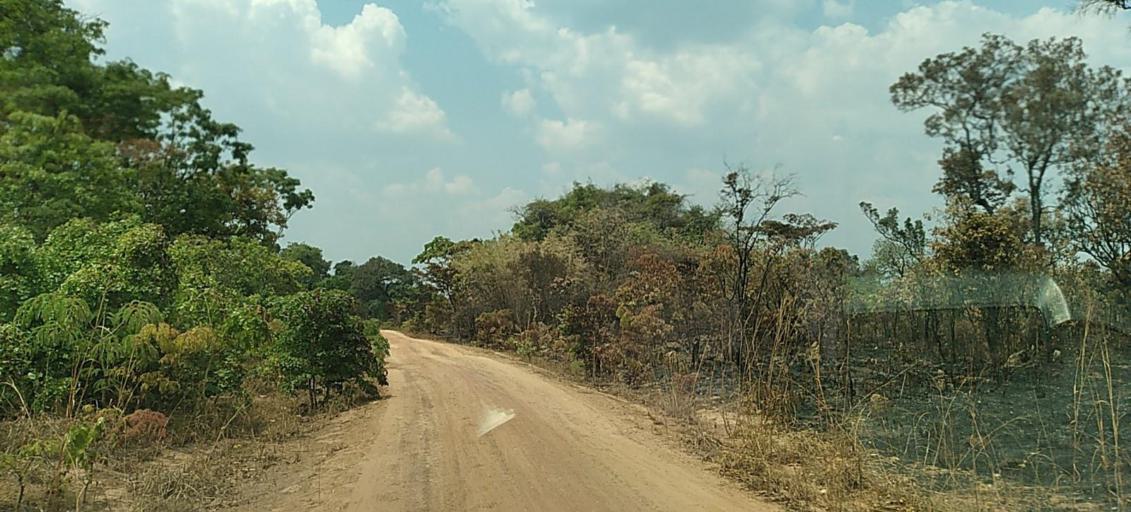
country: ZM
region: Copperbelt
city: Chingola
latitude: -12.6824
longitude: 27.7218
